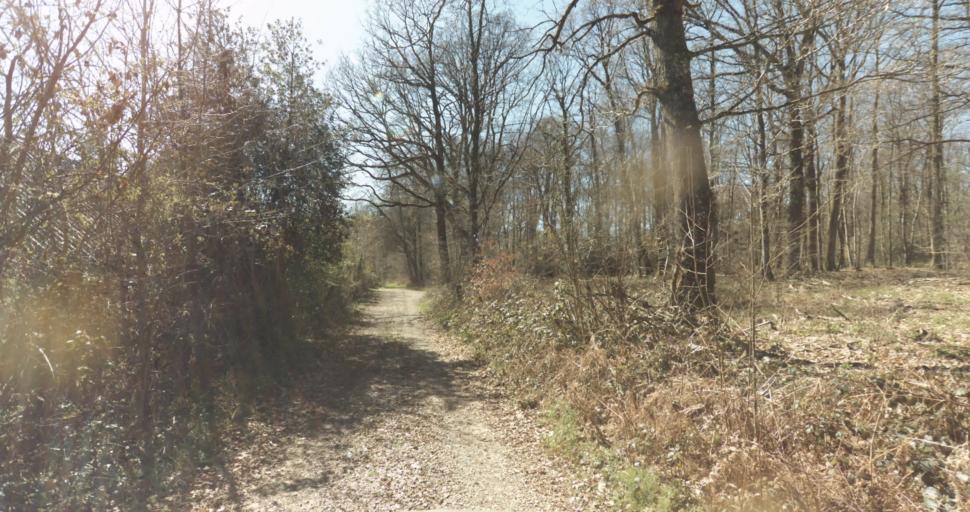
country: FR
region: Lower Normandy
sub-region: Departement du Calvados
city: Livarot
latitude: 48.9344
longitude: 0.0804
